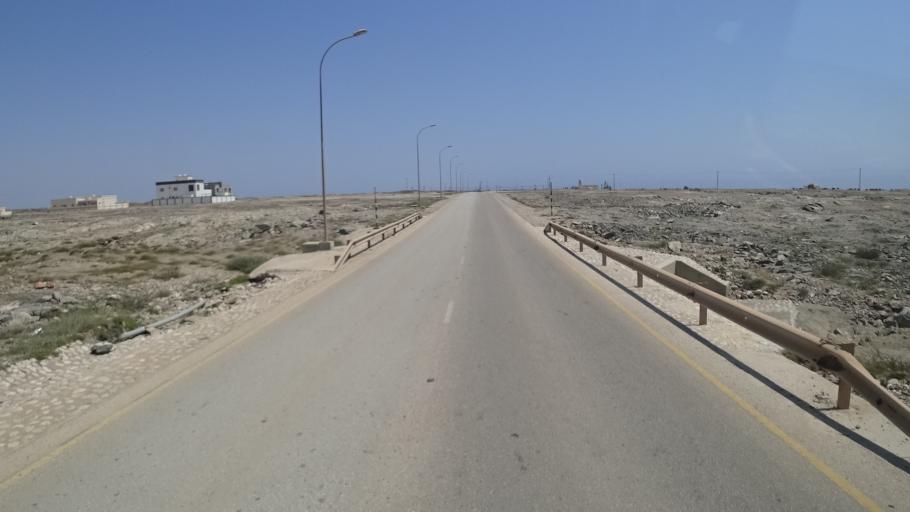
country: OM
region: Zufar
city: Salalah
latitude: 16.9670
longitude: 54.7349
